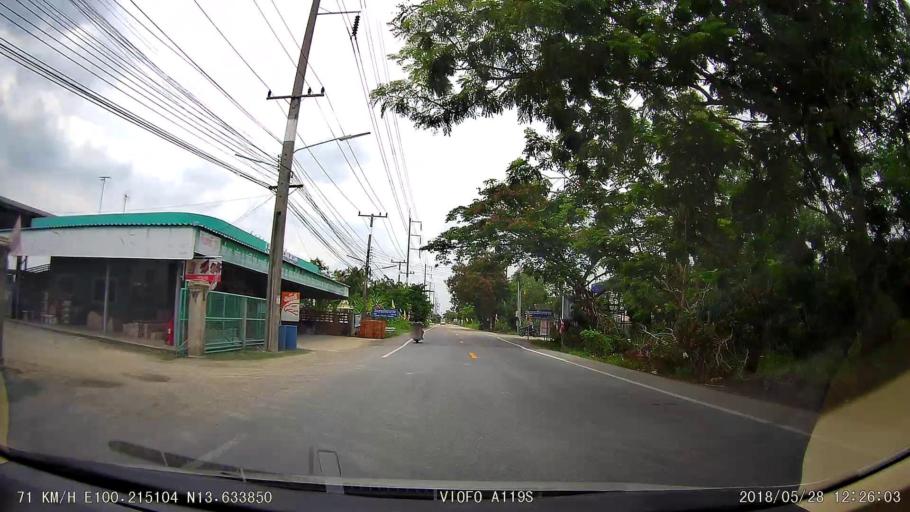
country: TH
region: Samut Sakhon
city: Krathum Baen
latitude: 13.6390
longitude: 100.2272
